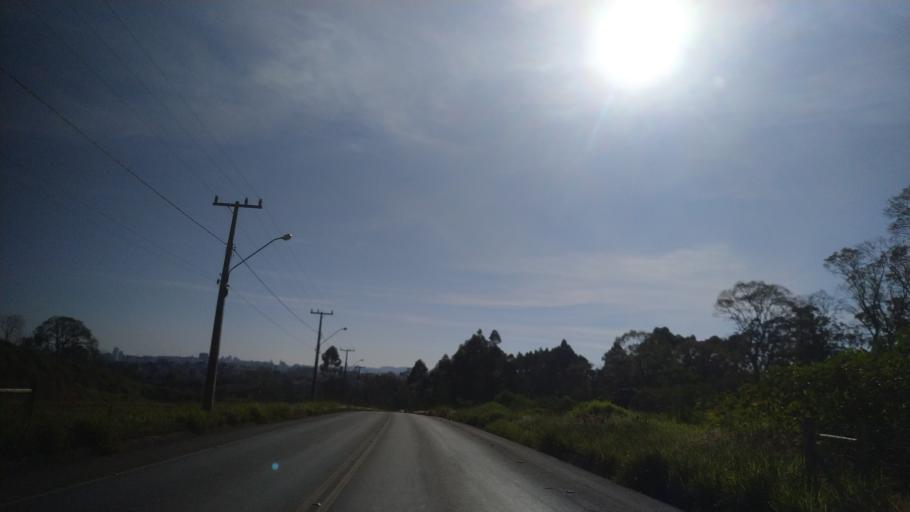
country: BR
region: Santa Catarina
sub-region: Chapeco
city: Chapeco
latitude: -27.1177
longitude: -52.6318
